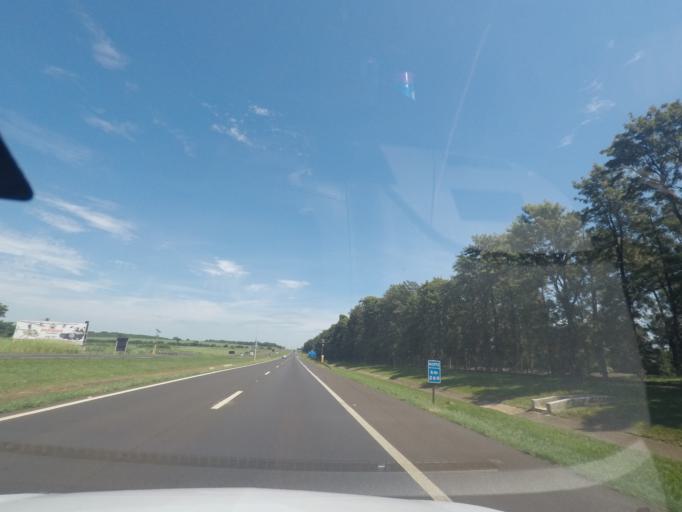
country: BR
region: Sao Paulo
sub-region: Araraquara
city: Araraquara
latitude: -21.8321
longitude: -48.1593
